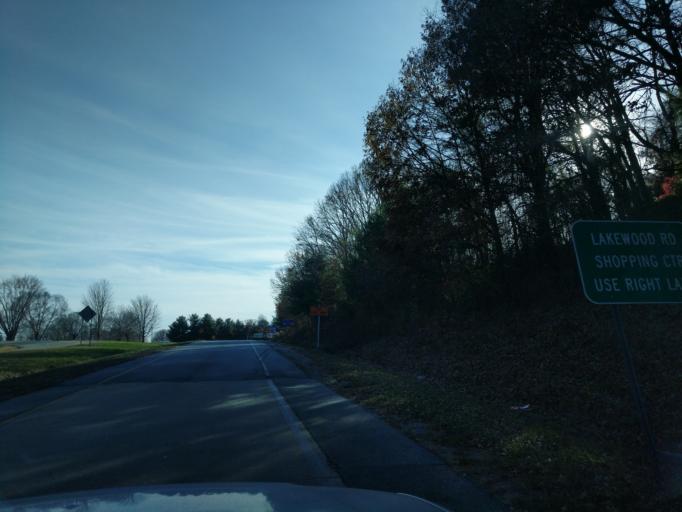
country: US
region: North Carolina
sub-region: Henderson County
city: Hendersonville
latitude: 35.3418
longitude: -82.4420
